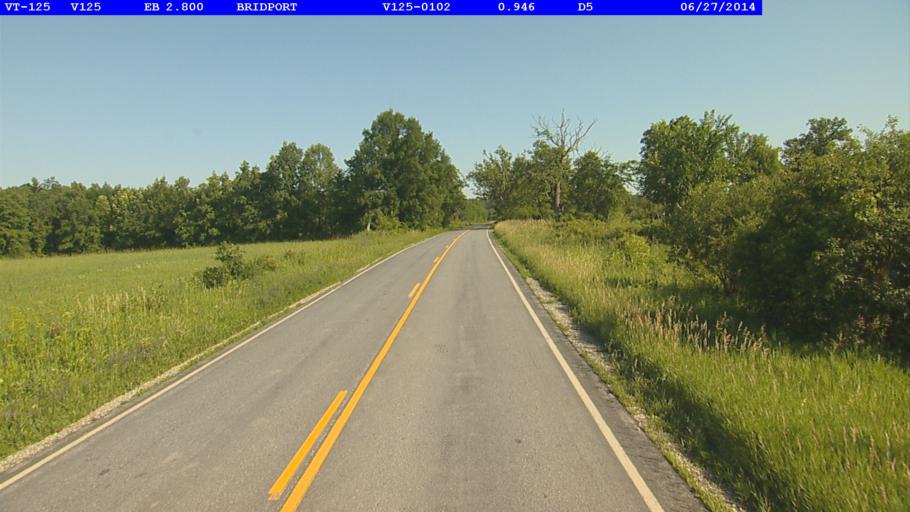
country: US
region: New York
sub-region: Essex County
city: Port Henry
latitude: 44.0088
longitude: -73.3861
